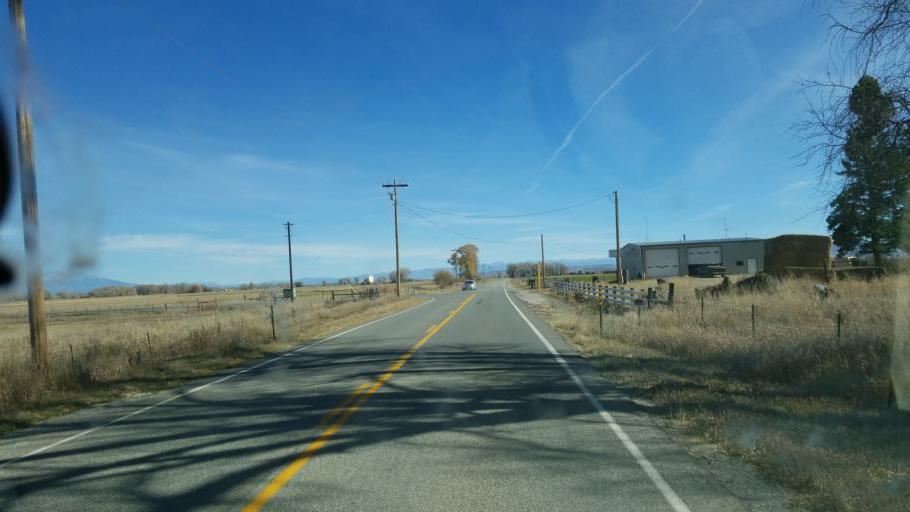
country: US
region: Colorado
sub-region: Conejos County
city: Conejos
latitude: 37.2837
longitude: -106.0392
